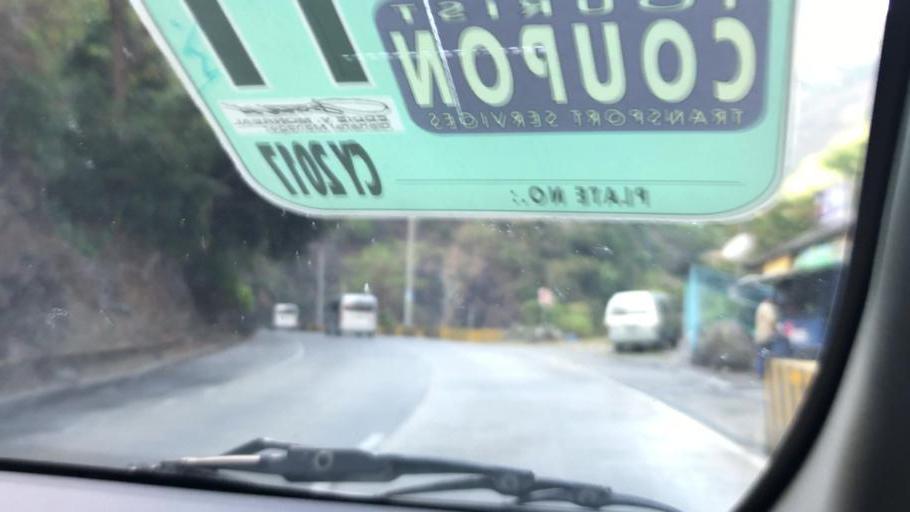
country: PH
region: Cordillera
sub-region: Province of Benguet
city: Tuba
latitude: 16.3251
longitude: 120.6142
